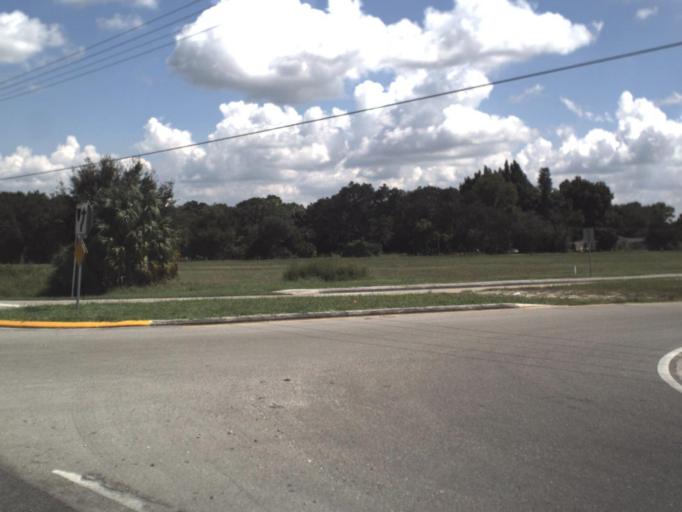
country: US
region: Florida
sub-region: Lee County
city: Palmona Park
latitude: 26.6753
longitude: -81.9241
